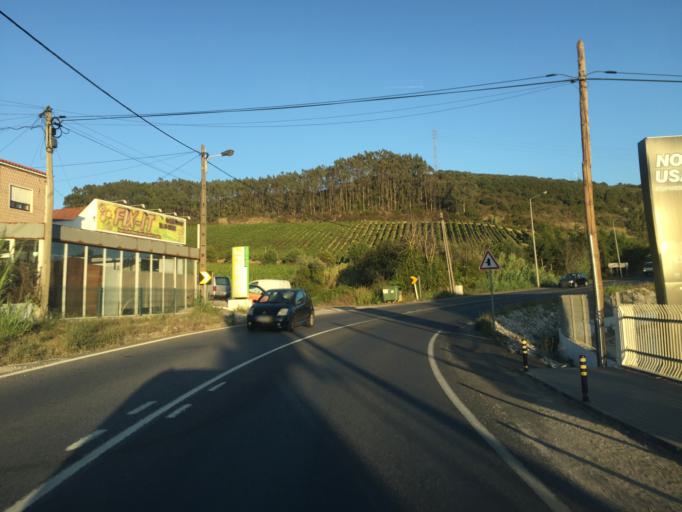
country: PT
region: Lisbon
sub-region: Torres Vedras
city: Torres Vedras
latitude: 39.0699
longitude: -9.2424
